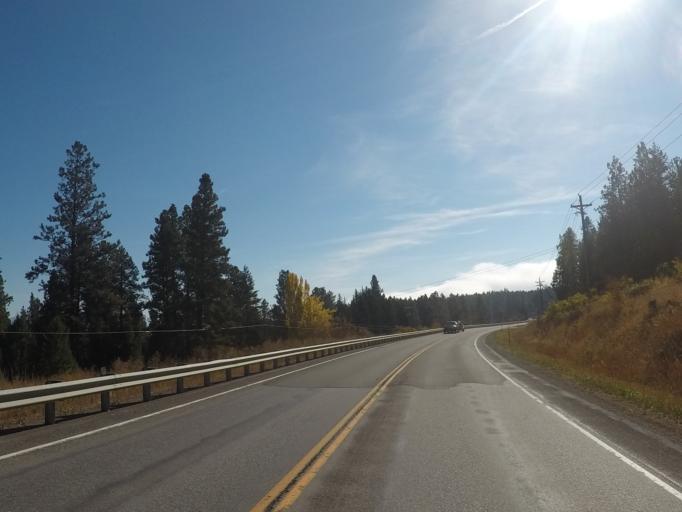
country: US
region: Montana
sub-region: Flathead County
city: Somers
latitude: 48.0538
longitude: -114.2345
